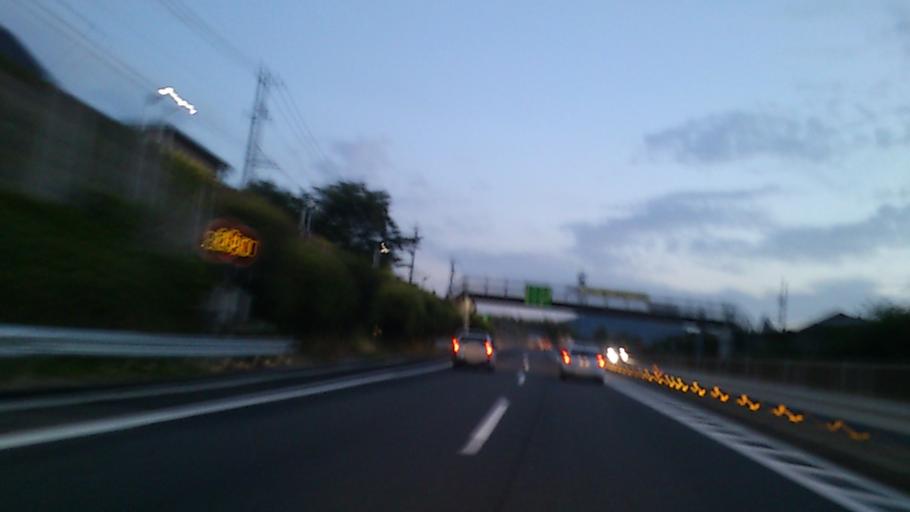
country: JP
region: Gifu
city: Tajimi
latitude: 35.3457
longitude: 137.1019
